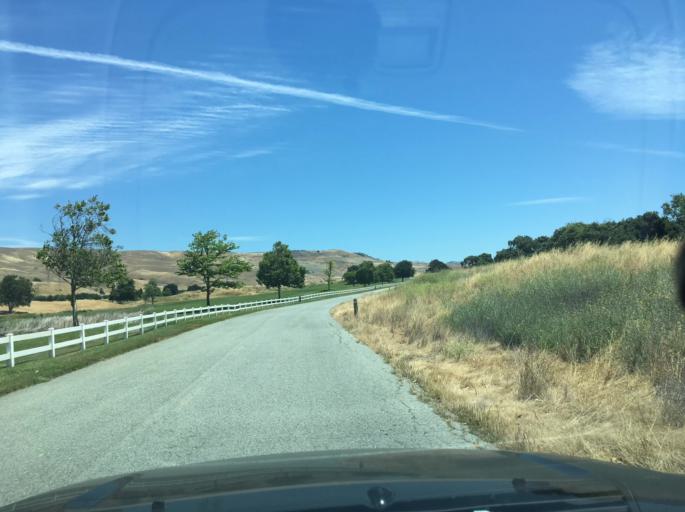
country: US
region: California
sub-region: Santa Clara County
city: Morgan Hill
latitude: 37.1906
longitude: -121.7046
